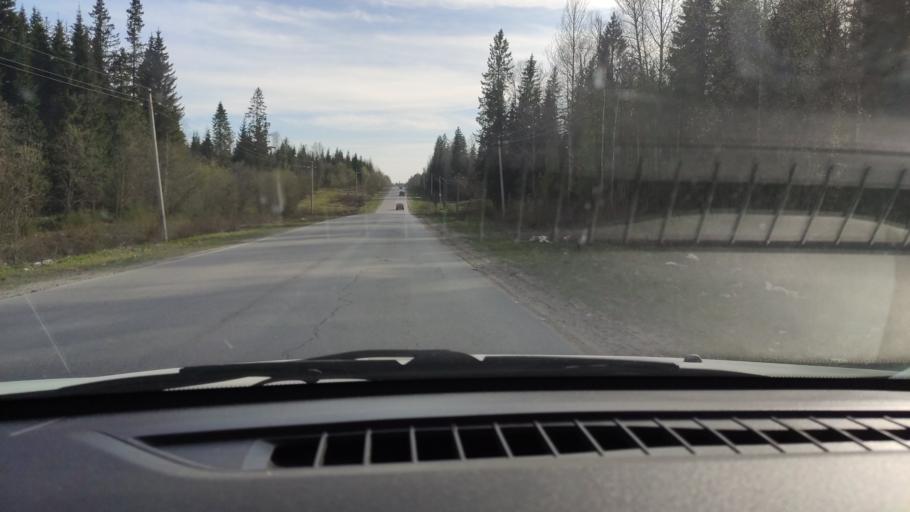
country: RU
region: Perm
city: Novyye Lyady
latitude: 57.9508
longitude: 56.5095
